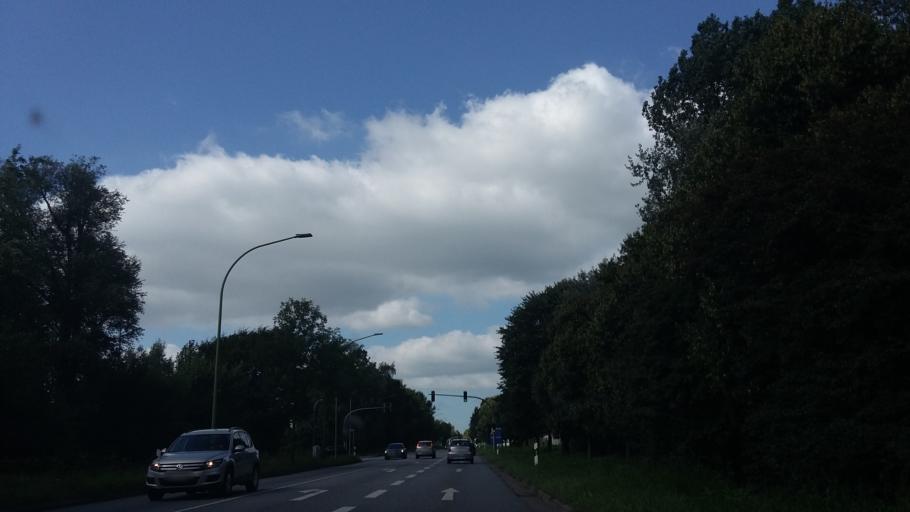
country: DE
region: Lower Saxony
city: Loxstedt
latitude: 53.4913
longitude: 8.6024
